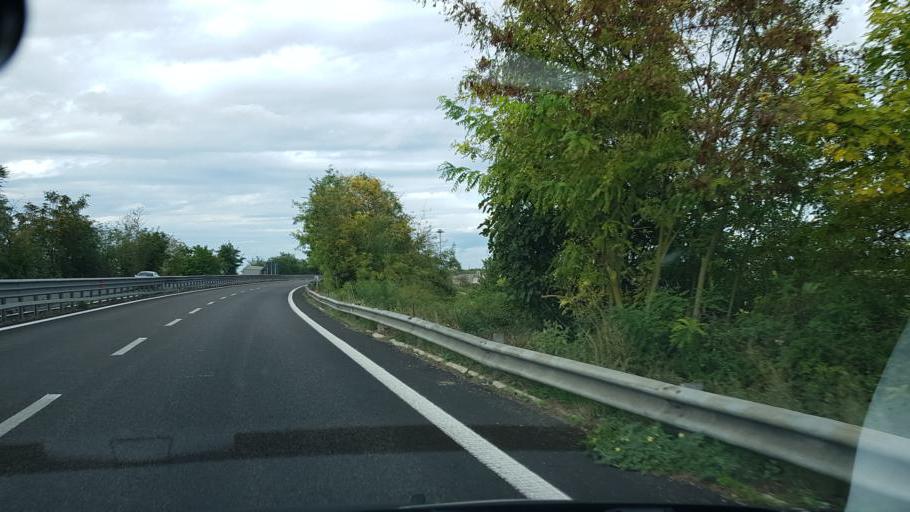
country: IT
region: Apulia
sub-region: Provincia di Lecce
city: Castromediano
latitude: 40.3262
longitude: 18.1854
